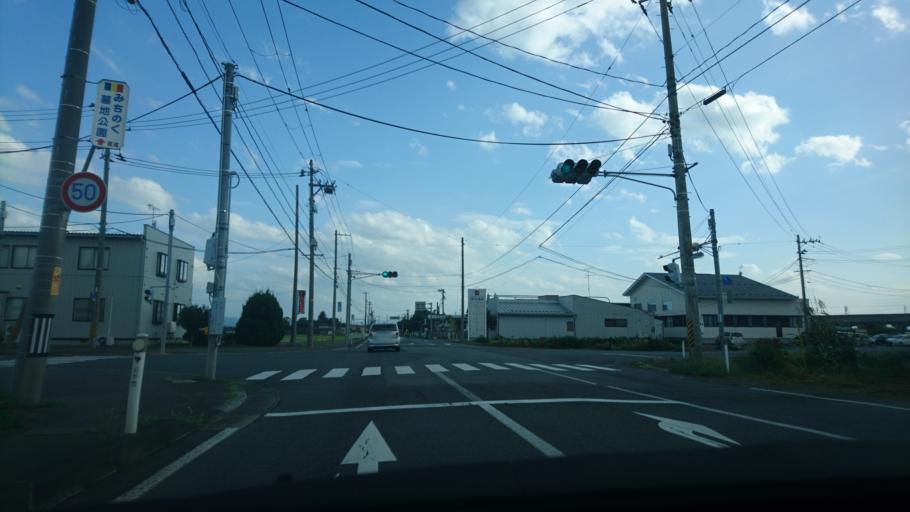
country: JP
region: Iwate
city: Mizusawa
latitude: 39.1778
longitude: 141.1770
